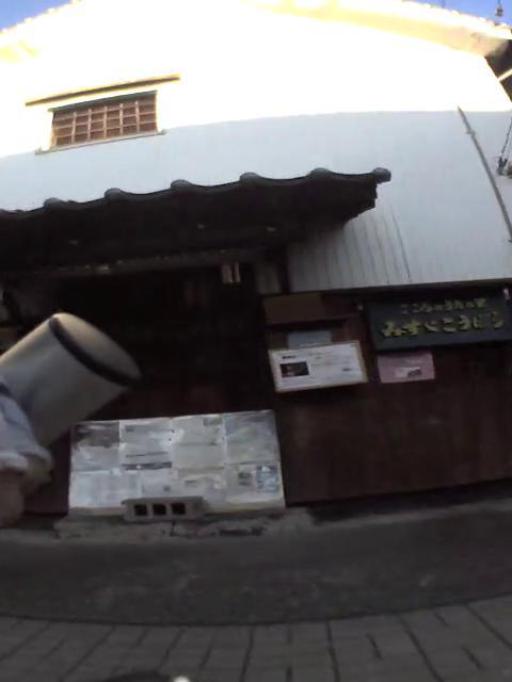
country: JP
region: Yamaguchi
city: Nagato
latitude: 34.3915
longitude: 131.1985
